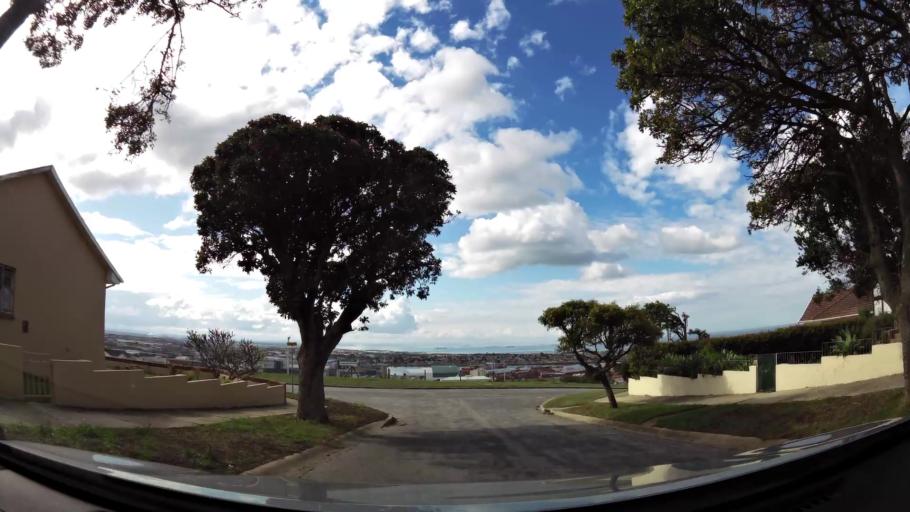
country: ZA
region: Eastern Cape
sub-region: Nelson Mandela Bay Metropolitan Municipality
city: Port Elizabeth
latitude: -33.9415
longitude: 25.5847
